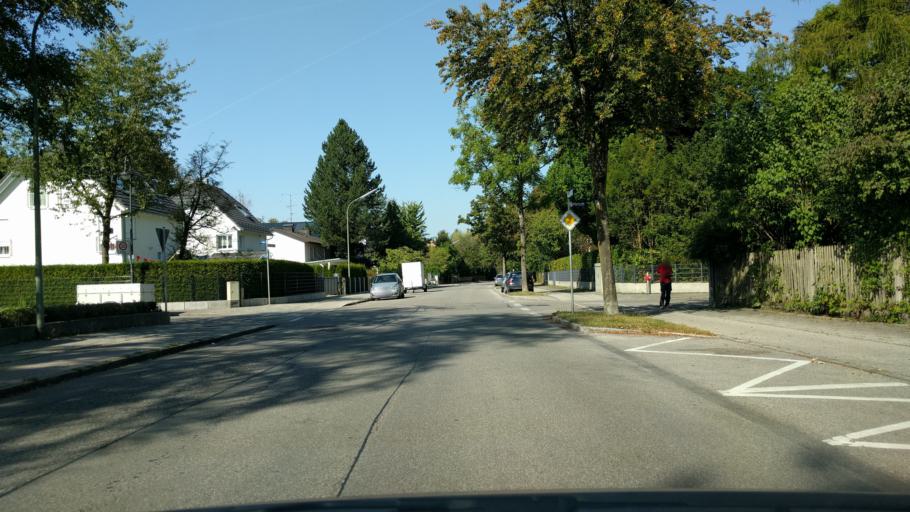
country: DE
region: Bavaria
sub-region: Upper Bavaria
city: Pullach im Isartal
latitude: 48.0626
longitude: 11.5187
